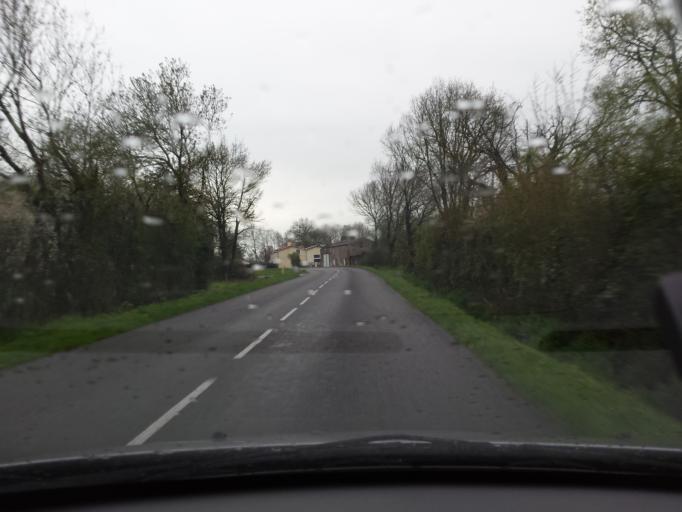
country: FR
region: Pays de la Loire
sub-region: Departement de la Vendee
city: Chauche
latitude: 46.7881
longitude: -1.3061
